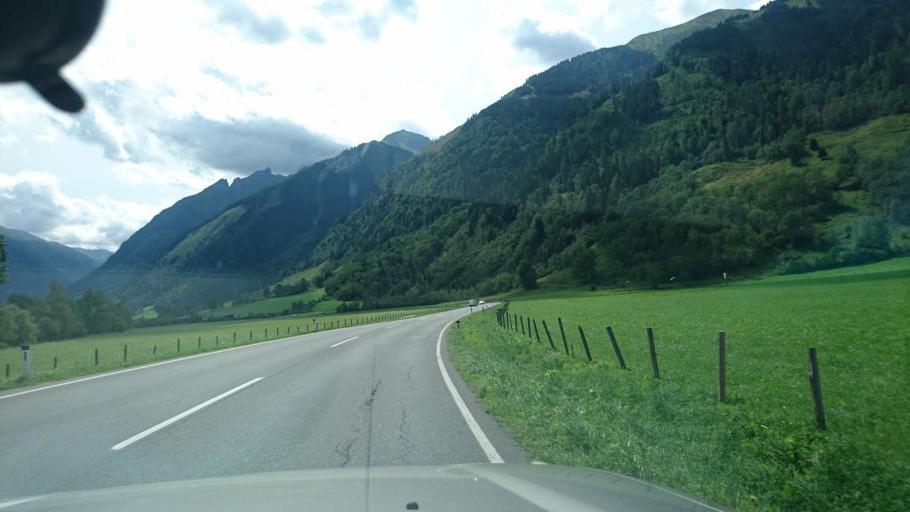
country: AT
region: Salzburg
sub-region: Politischer Bezirk Zell am See
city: Bruck an der Grossglocknerstrasse
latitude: 47.2444
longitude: 12.8268
